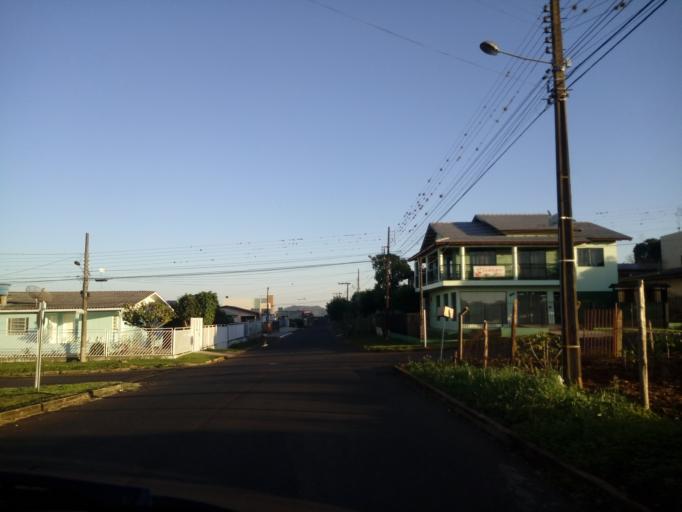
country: BR
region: Santa Catarina
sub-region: Chapeco
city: Chapeco
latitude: -27.0806
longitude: -52.6315
